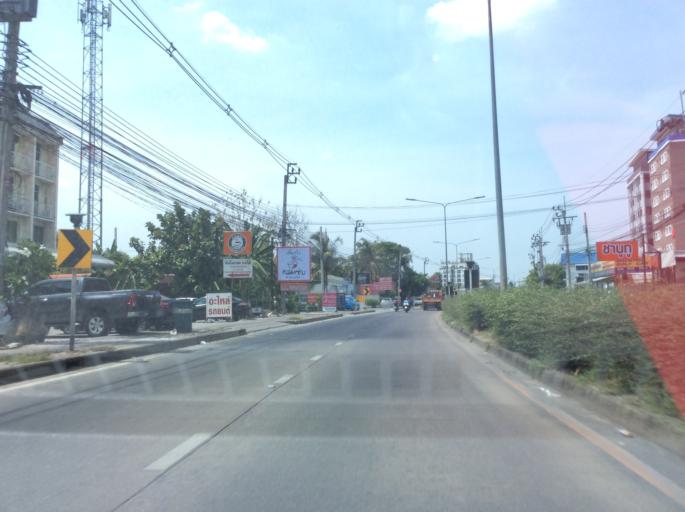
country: TH
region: Nonthaburi
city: Pak Kret
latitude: 13.8933
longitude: 100.5162
